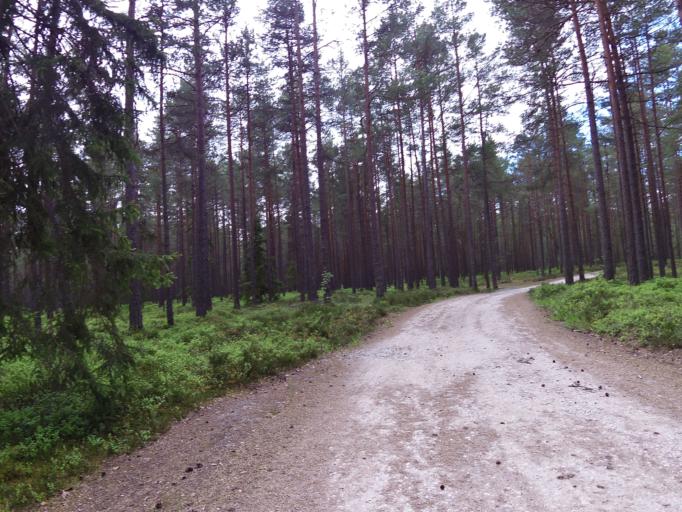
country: EE
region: Harju
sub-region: Paldiski linn
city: Paldiski
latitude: 59.2489
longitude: 23.7496
